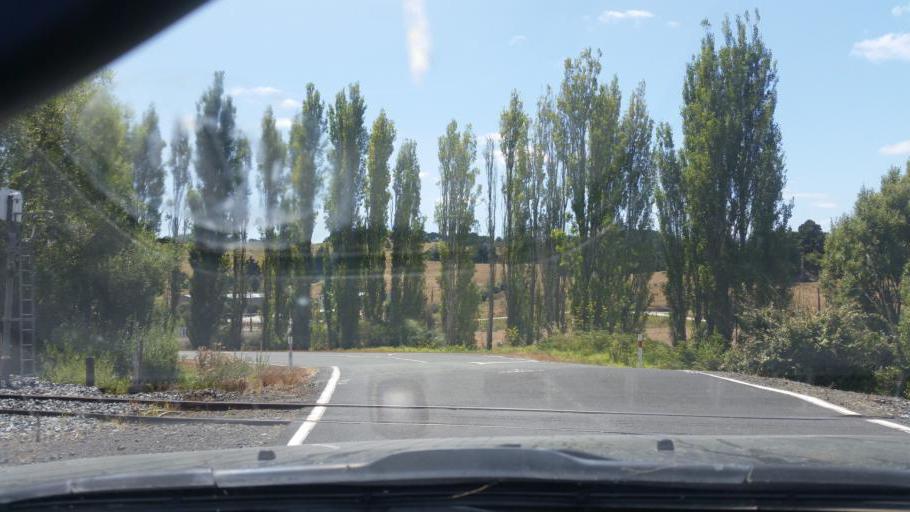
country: NZ
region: Auckland
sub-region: Auckland
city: Wellsford
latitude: -36.1231
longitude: 174.3330
